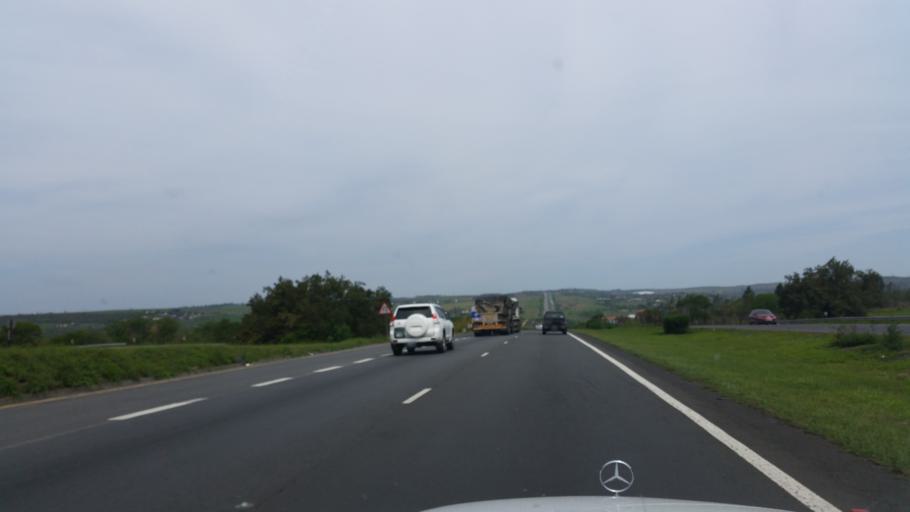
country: ZA
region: KwaZulu-Natal
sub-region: uMgungundlovu District Municipality
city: Pietermaritzburg
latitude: -29.6602
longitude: 30.4557
